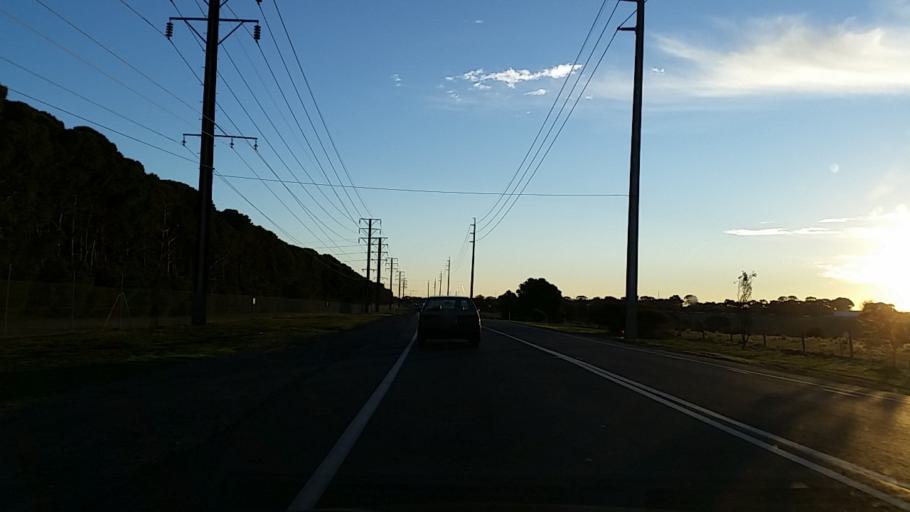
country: AU
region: South Australia
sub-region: Onkaparinga
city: Bedford Park
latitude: -35.0546
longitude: 138.5668
